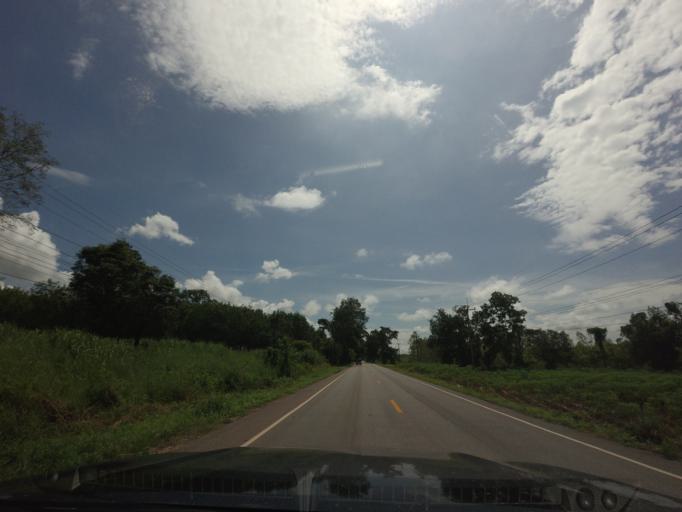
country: TH
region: Nong Khai
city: Pho Tak
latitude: 17.7952
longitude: 102.3541
